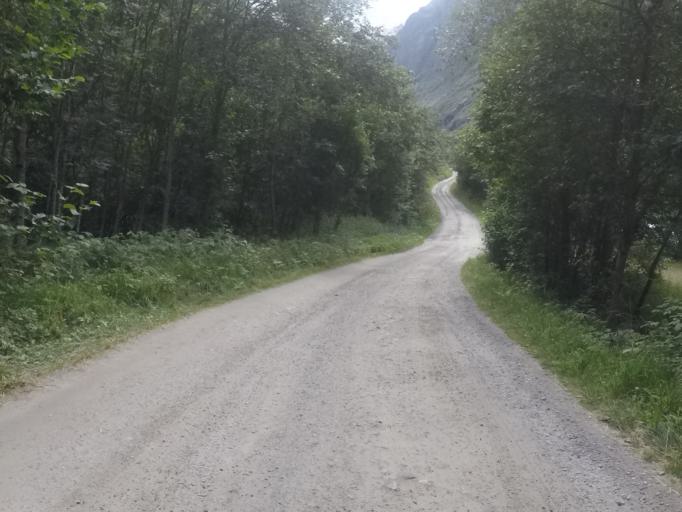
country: NO
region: Sogn og Fjordane
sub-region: Stryn
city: Stryn
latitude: 61.7603
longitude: 7.0412
